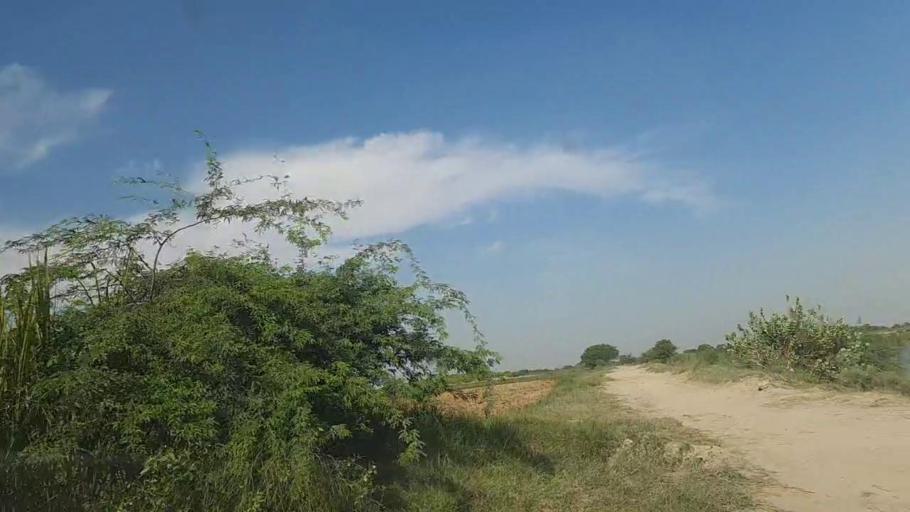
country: PK
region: Sindh
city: Bulri
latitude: 24.8153
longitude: 68.2658
